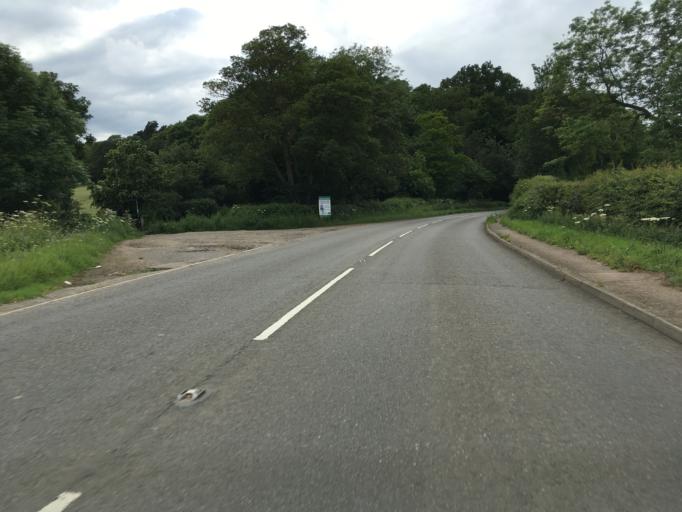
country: GB
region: England
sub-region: Central Bedfordshire
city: Woburn
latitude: 51.9956
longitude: -0.6316
